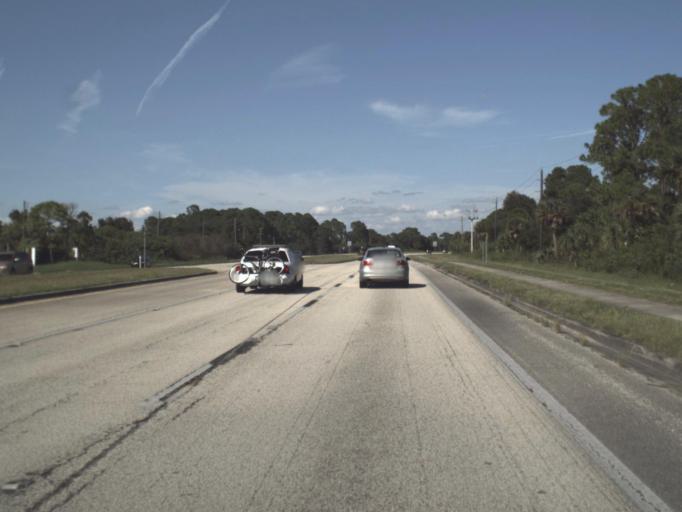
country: US
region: Florida
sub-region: Sarasota County
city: North Port
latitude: 26.9872
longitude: -82.2057
